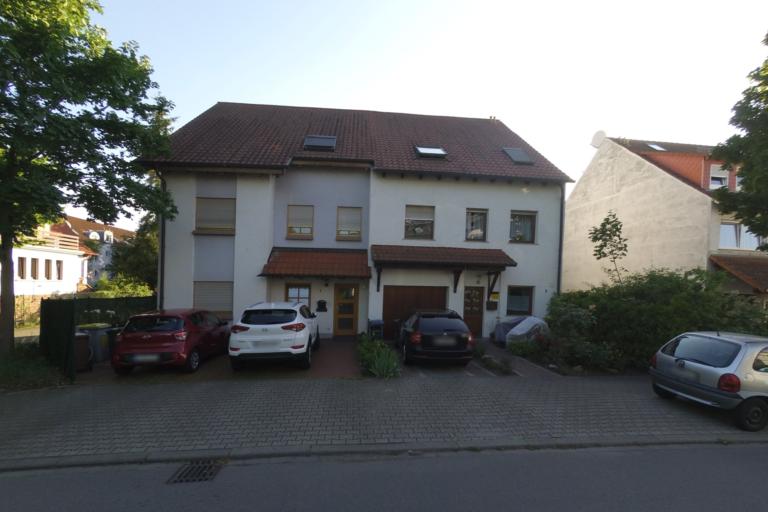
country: DE
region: Rheinland-Pfalz
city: Altrip
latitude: 49.4535
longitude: 8.4787
